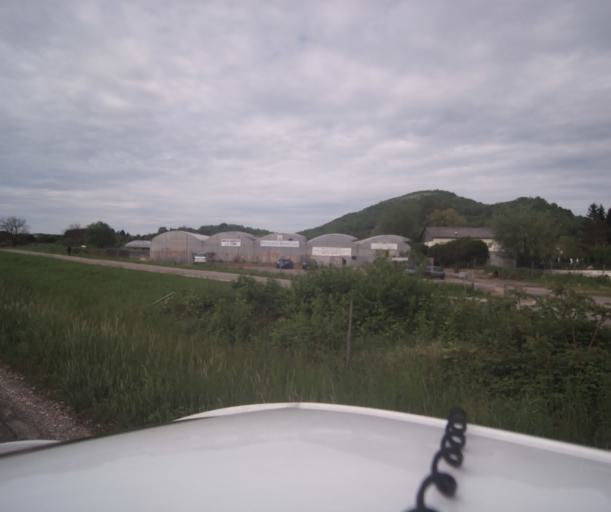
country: FR
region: Franche-Comte
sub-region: Departement du Doubs
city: Beure
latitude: 47.2140
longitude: 5.9880
